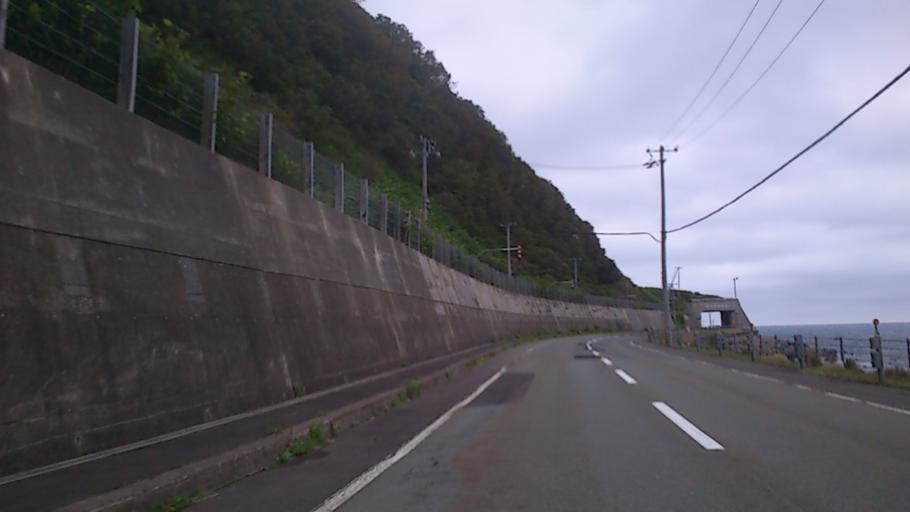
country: JP
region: Hokkaido
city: Iwanai
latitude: 42.6808
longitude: 139.9073
